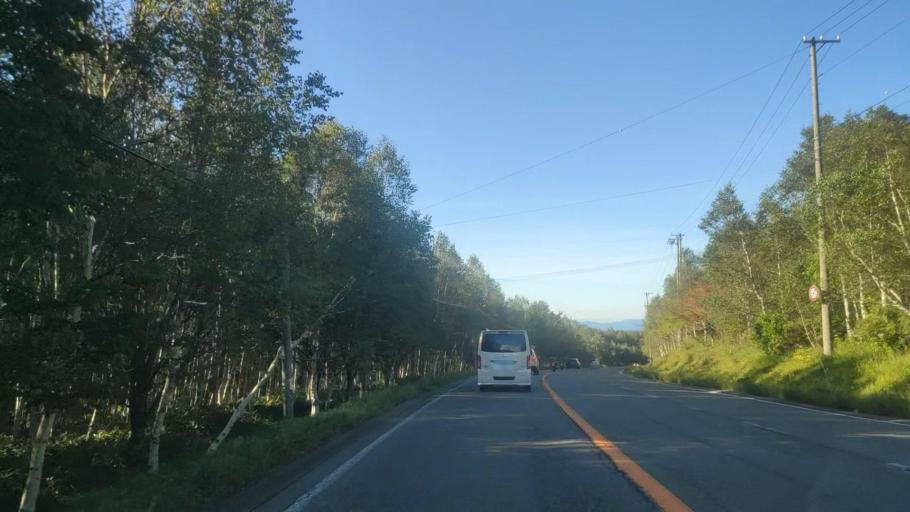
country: JP
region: Nagano
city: Kamimaruko
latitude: 36.1564
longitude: 138.2793
